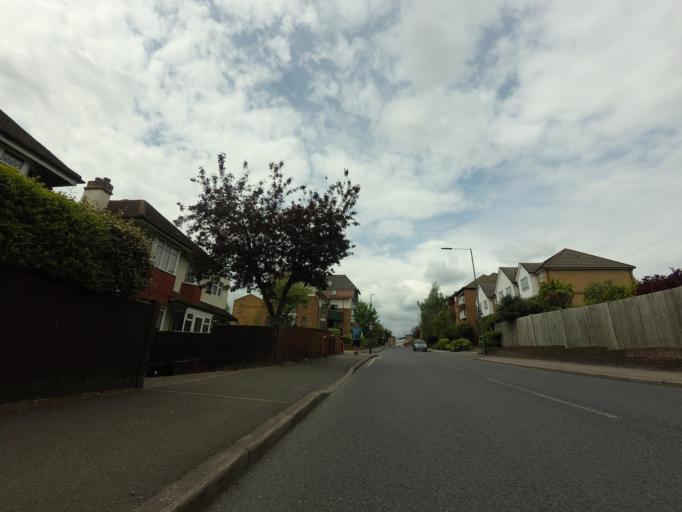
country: GB
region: England
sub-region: Greater London
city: Sidcup
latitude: 51.4226
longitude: 0.1094
